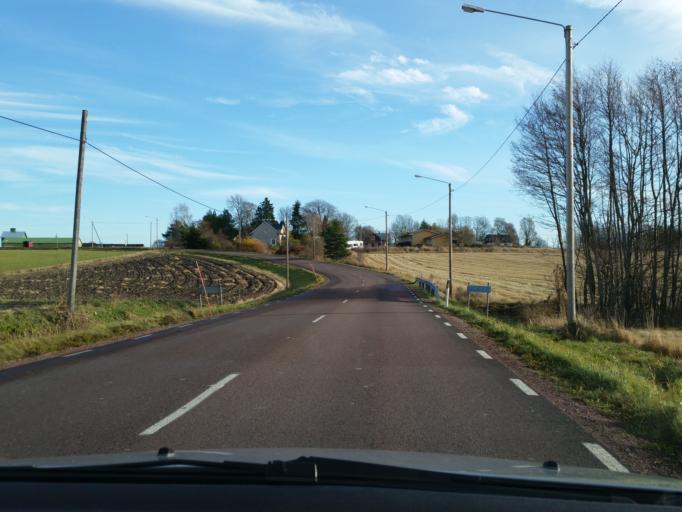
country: AX
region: Alands landsbygd
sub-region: Finstroem
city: Finstroem
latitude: 60.3091
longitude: 19.9755
